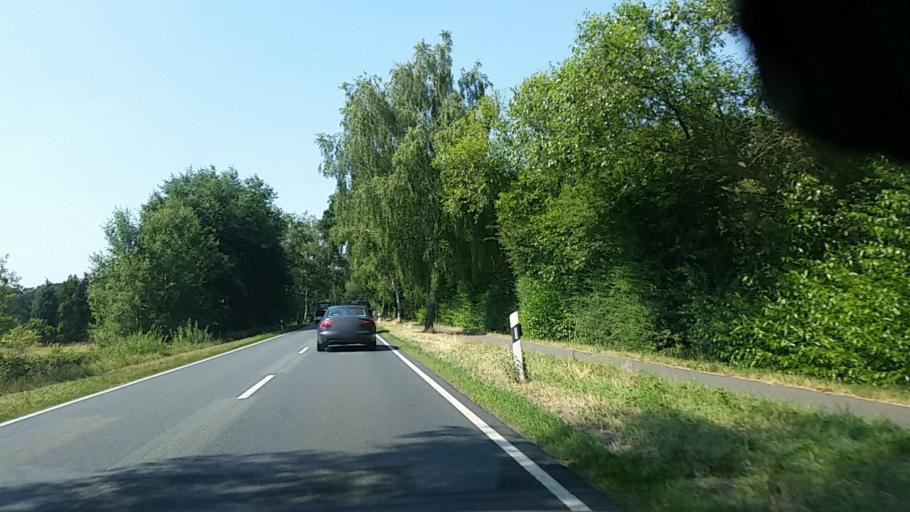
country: DE
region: Lower Saxony
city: Ottersberg
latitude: 53.0737
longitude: 9.1642
